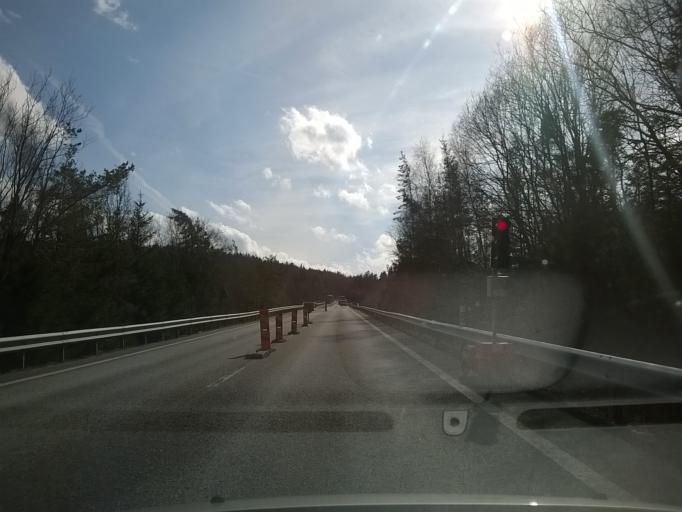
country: SE
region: Vaestra Goetaland
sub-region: Orust
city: Henan
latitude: 58.2965
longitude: 11.7017
